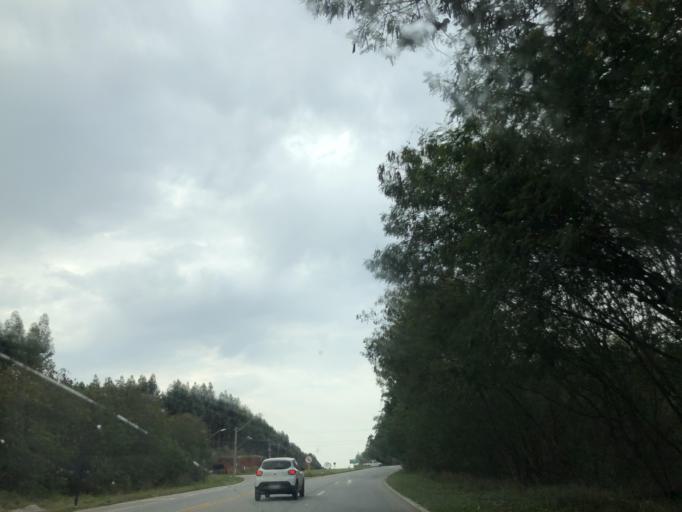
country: BR
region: Sao Paulo
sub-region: Salto De Pirapora
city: Salto de Pirapora
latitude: -23.6719
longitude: -47.6017
